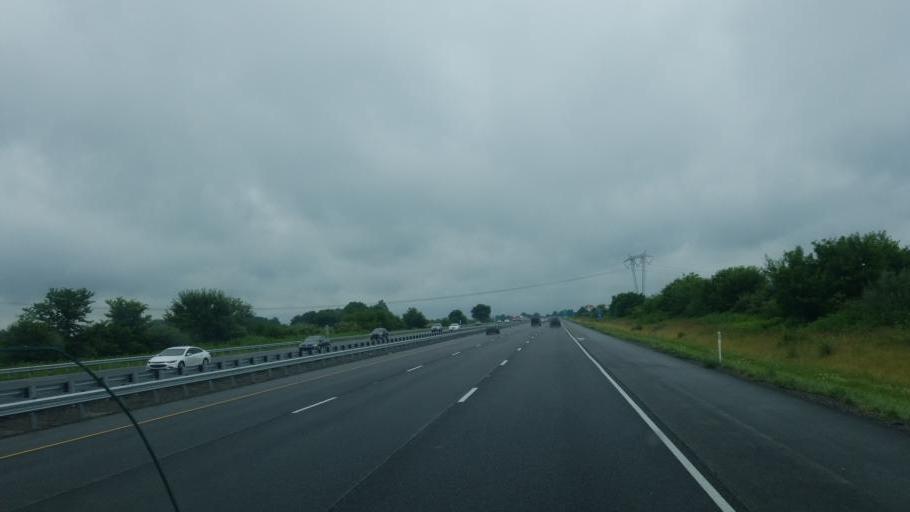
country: US
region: Indiana
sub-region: Madison County
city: Ingalls
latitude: 39.9919
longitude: -85.8095
